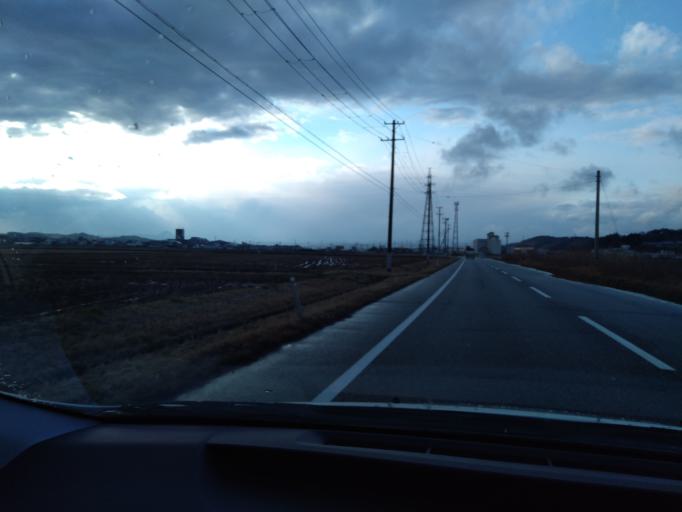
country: JP
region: Iwate
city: Ichinoseki
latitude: 38.7987
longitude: 141.0760
